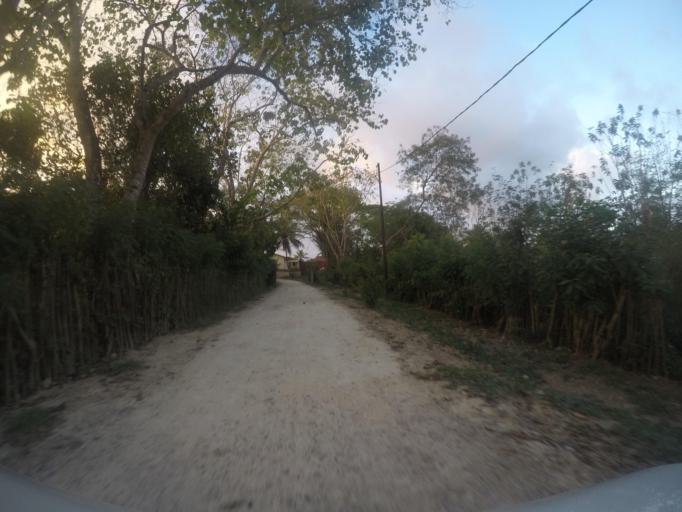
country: TL
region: Lautem
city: Lospalos
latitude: -8.4999
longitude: 127.0006
